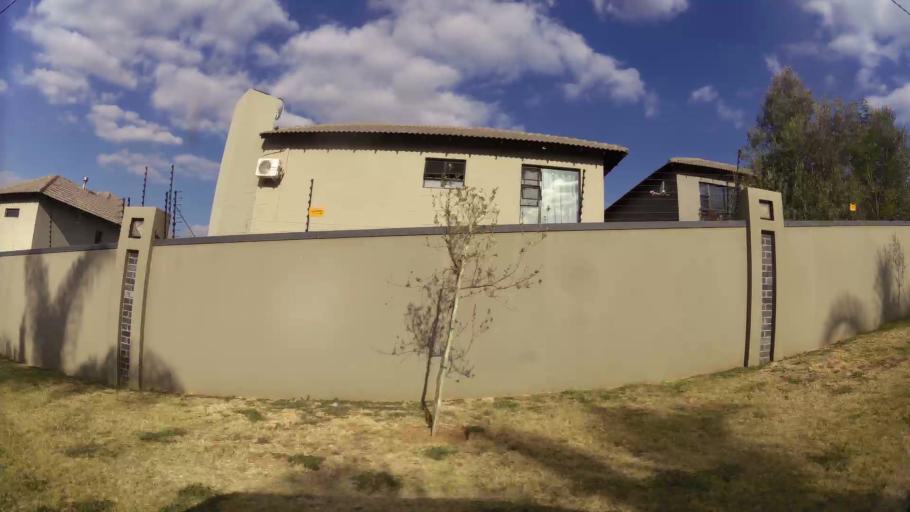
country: ZA
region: Gauteng
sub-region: City of Johannesburg Metropolitan Municipality
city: Diepsloot
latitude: -25.9989
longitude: 28.0197
